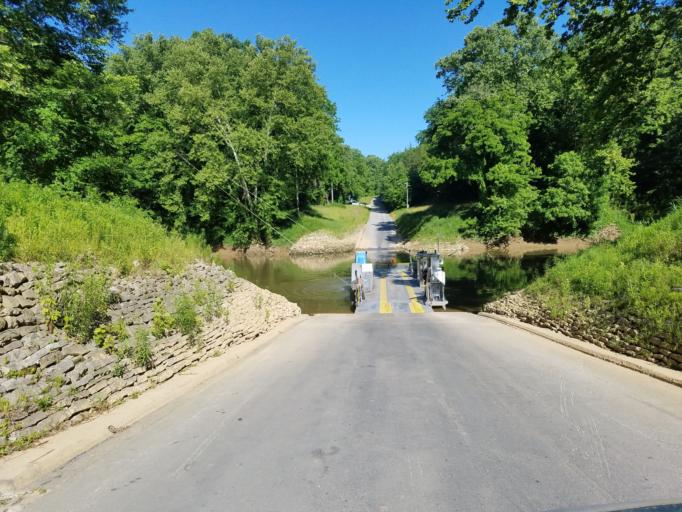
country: US
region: Kentucky
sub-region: Edmonson County
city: Brownsville
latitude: 37.1787
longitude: -86.1102
